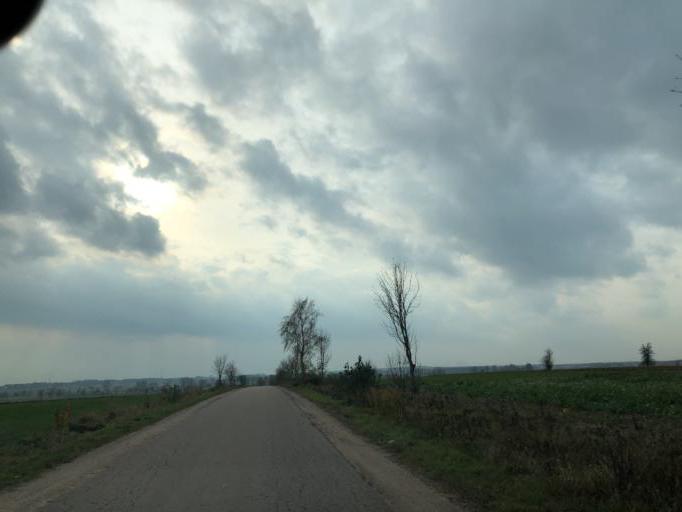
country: PL
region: Podlasie
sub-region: Powiat lomzynski
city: Sniadowo
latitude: 53.1266
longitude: 21.9658
